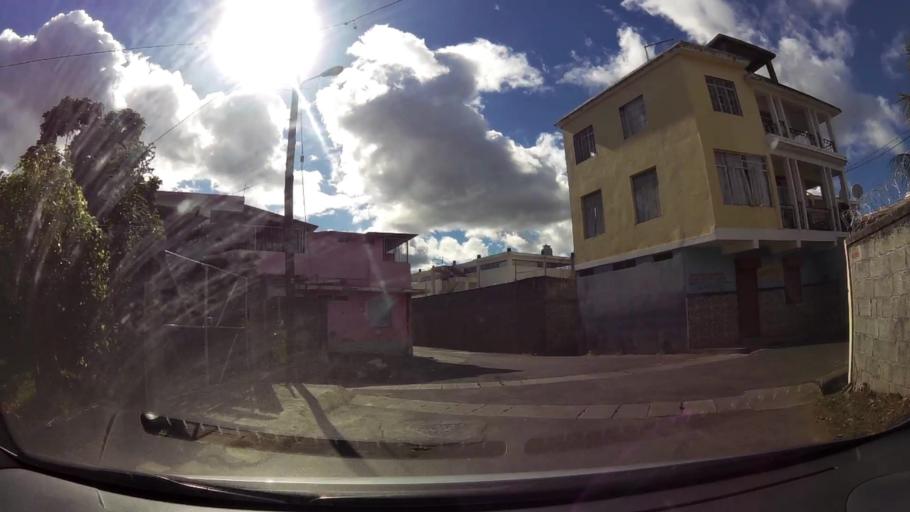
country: MU
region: Pamplemousses
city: Le Hochet
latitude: -20.1476
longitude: 57.5180
